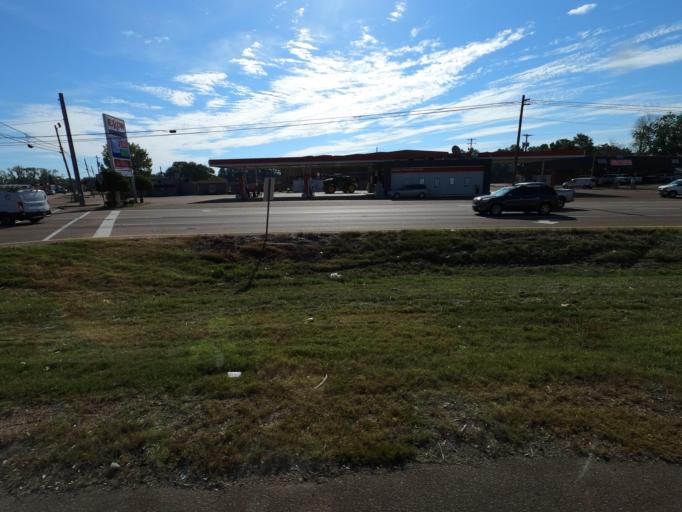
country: US
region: Tennessee
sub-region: Tipton County
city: Atoka
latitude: 35.4443
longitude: -89.7890
